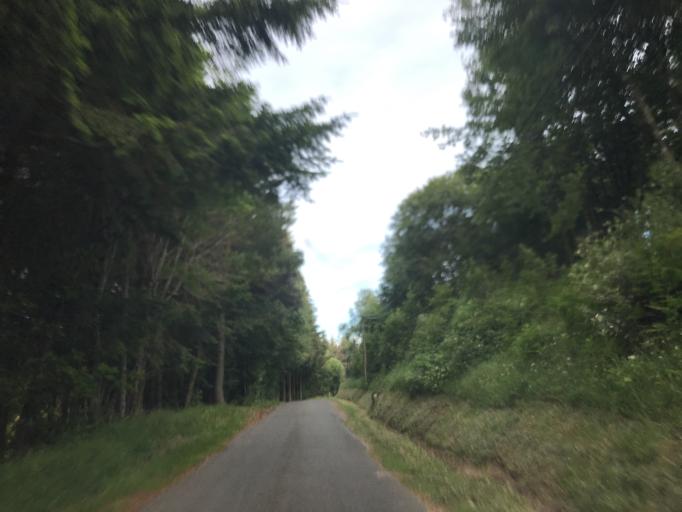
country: FR
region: Rhone-Alpes
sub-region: Departement de la Loire
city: Noiretable
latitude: 45.7823
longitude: 3.6882
